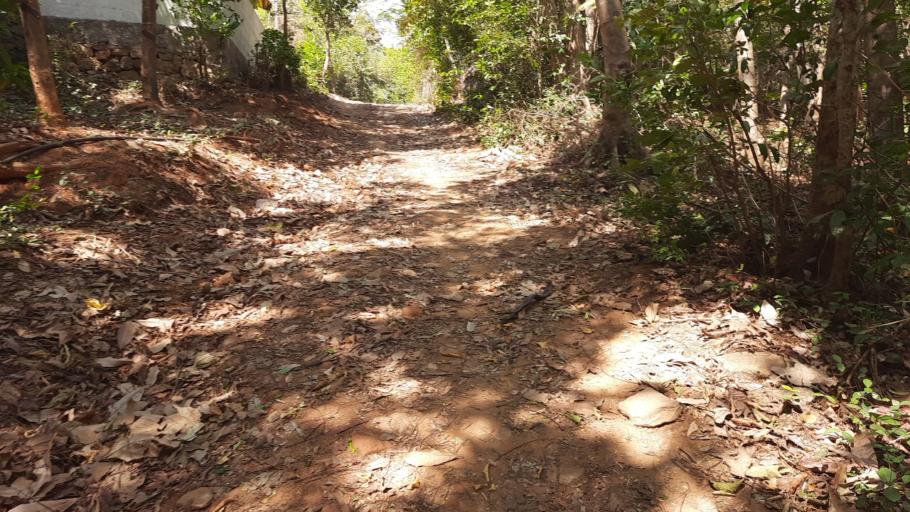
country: IN
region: Kerala
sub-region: Palakkad district
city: Ottappalam
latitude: 10.7186
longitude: 76.4766
